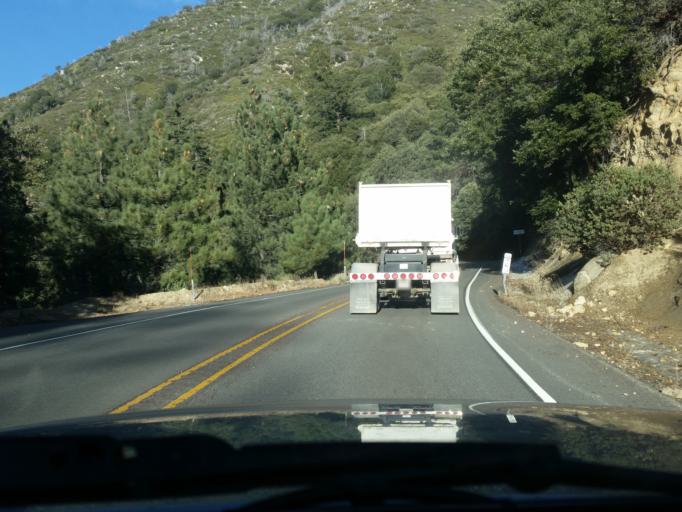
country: US
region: California
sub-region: San Bernardino County
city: Yucaipa
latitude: 34.1296
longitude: -116.9833
